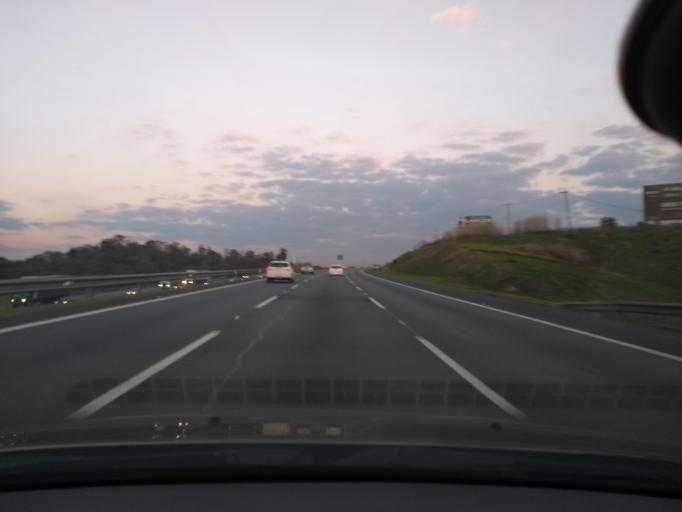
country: BR
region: Sao Paulo
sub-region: Louveira
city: Louveira
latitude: -23.1141
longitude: -46.9994
